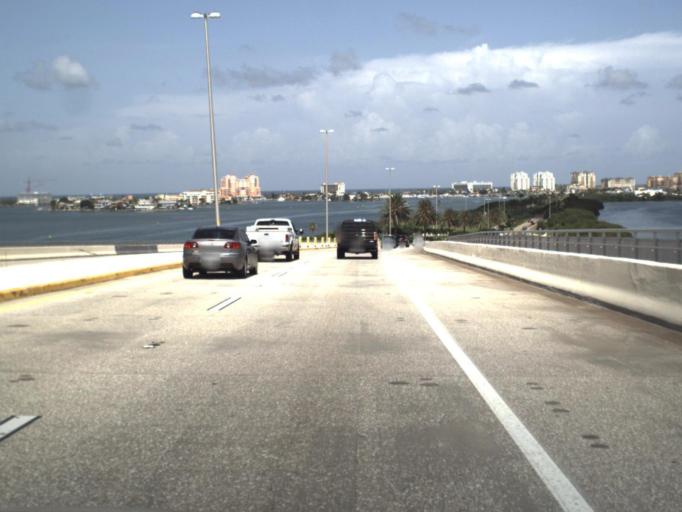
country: US
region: Florida
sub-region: Pinellas County
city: Clearwater
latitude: 27.9670
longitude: -82.8072
